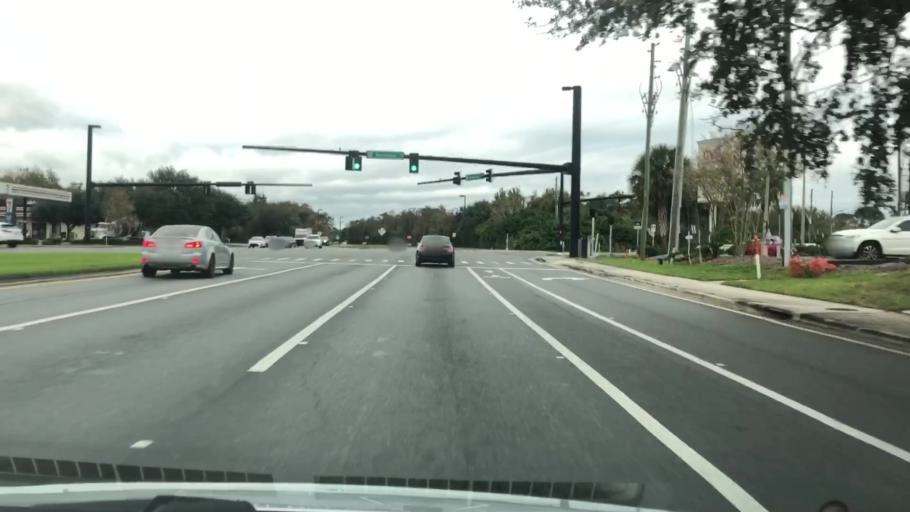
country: US
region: Florida
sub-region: Orange County
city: Conway
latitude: 28.4661
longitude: -81.2753
